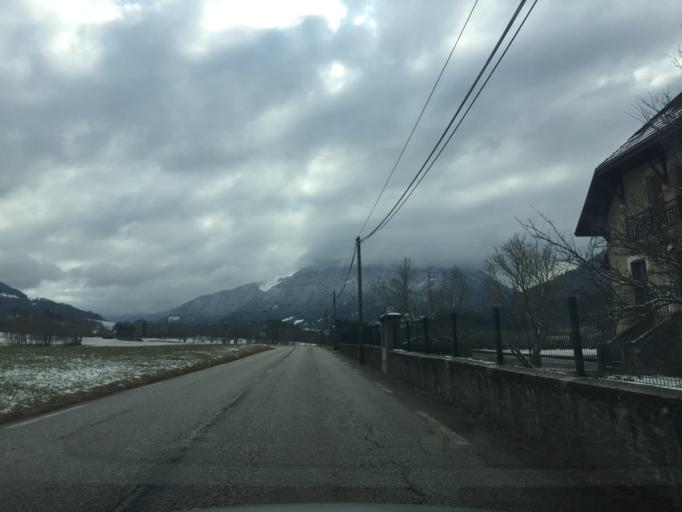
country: FR
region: Rhone-Alpes
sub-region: Departement de la Haute-Savoie
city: Gruffy
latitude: 45.7115
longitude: 6.1144
